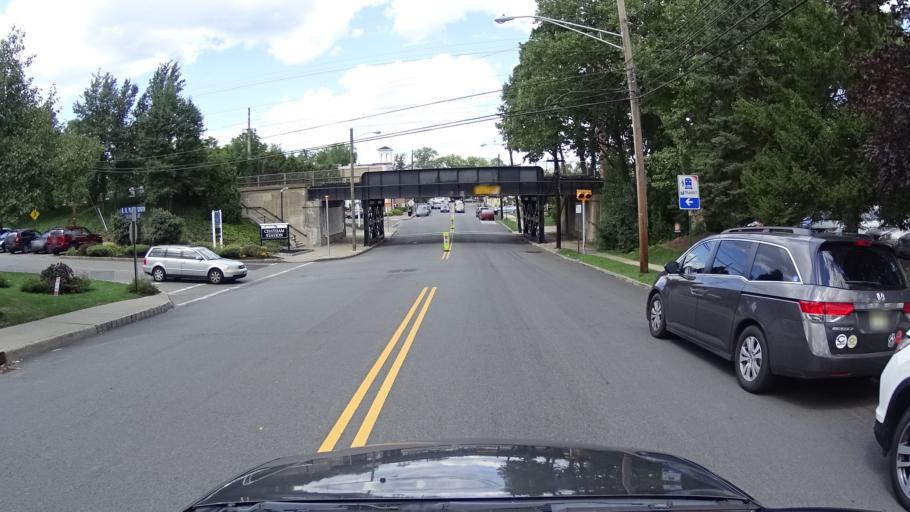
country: US
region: New Jersey
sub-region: Morris County
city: Chatham
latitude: 40.7393
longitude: -74.3839
